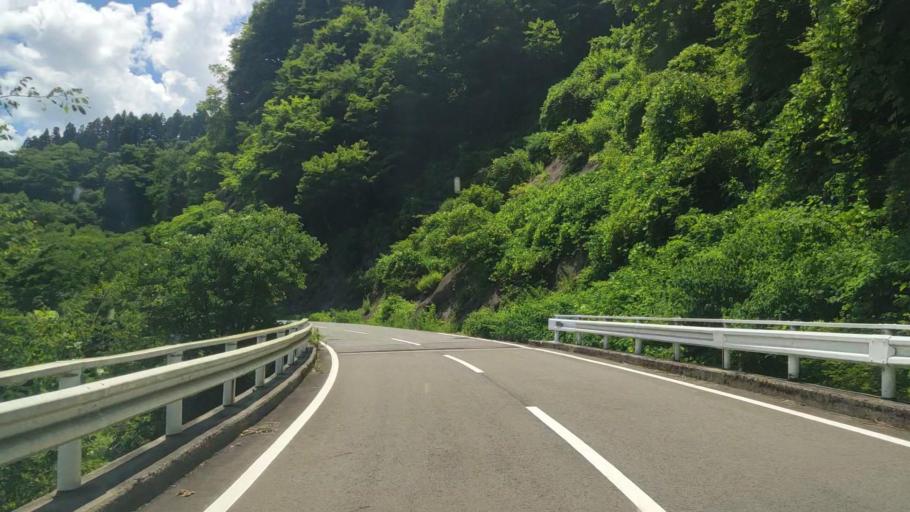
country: JP
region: Fukui
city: Ono
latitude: 35.8971
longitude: 136.5072
